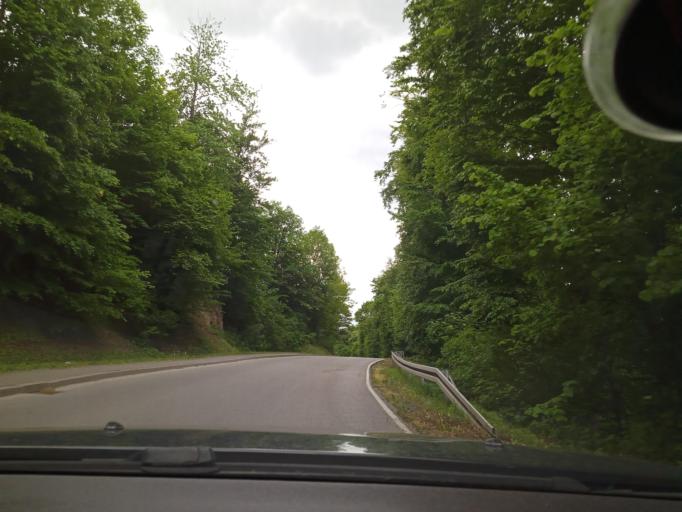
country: PL
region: Lesser Poland Voivodeship
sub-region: Powiat limanowski
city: Tymbark
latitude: 49.7839
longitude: 20.3320
